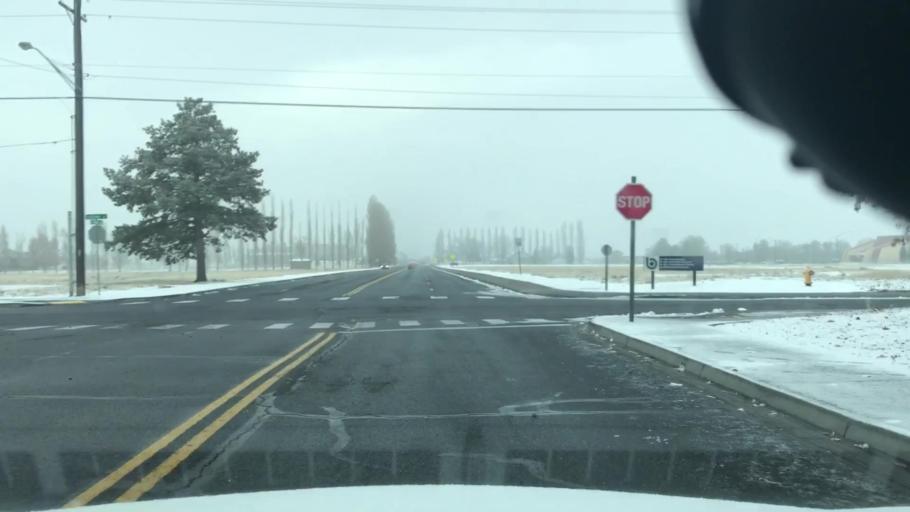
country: US
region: Washington
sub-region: Grant County
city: Moses Lake North
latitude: 47.1885
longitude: -119.3227
